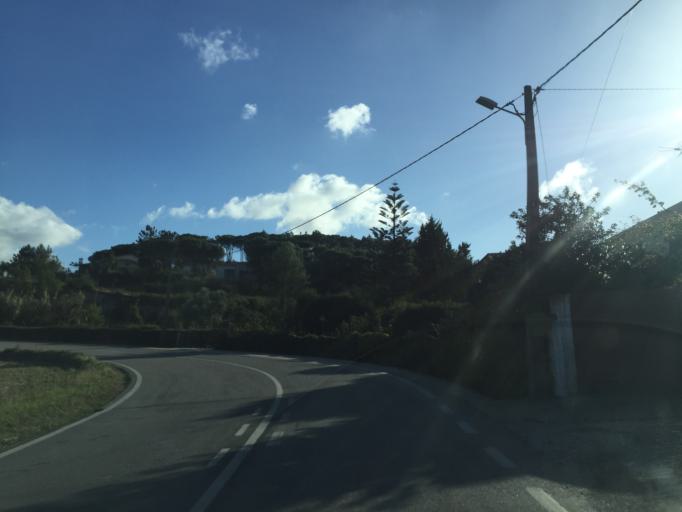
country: PT
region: Coimbra
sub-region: Figueira da Foz
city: Tavarede
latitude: 40.1977
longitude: -8.8347
